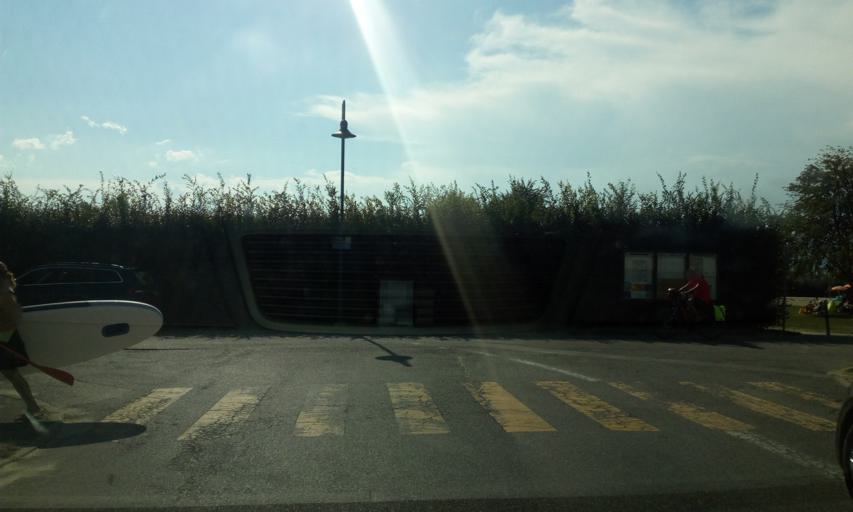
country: CH
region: Neuchatel
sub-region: Neuchatel District
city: Neuchatel
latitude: 46.9224
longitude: 6.9547
